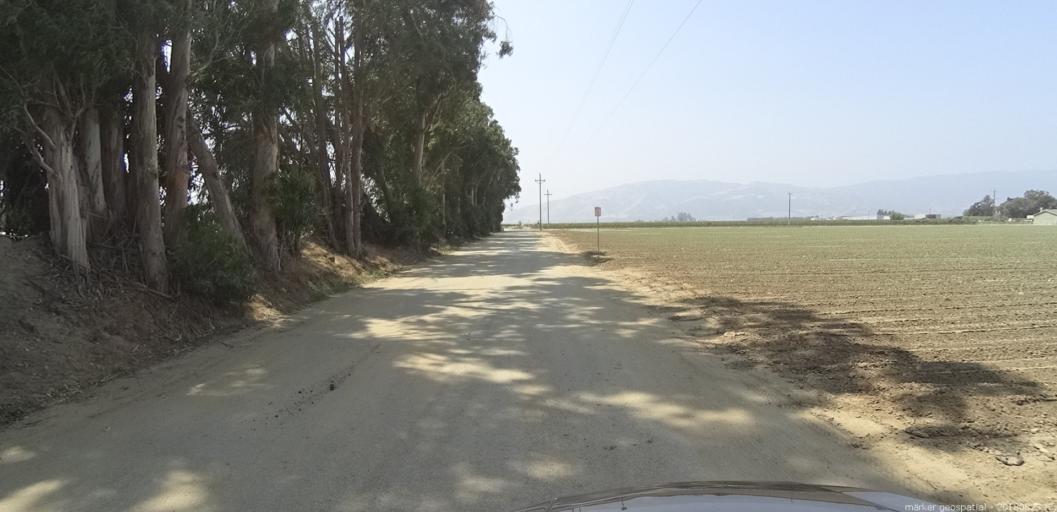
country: US
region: California
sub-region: Monterey County
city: Greenfield
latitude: 36.3266
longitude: -121.2569
